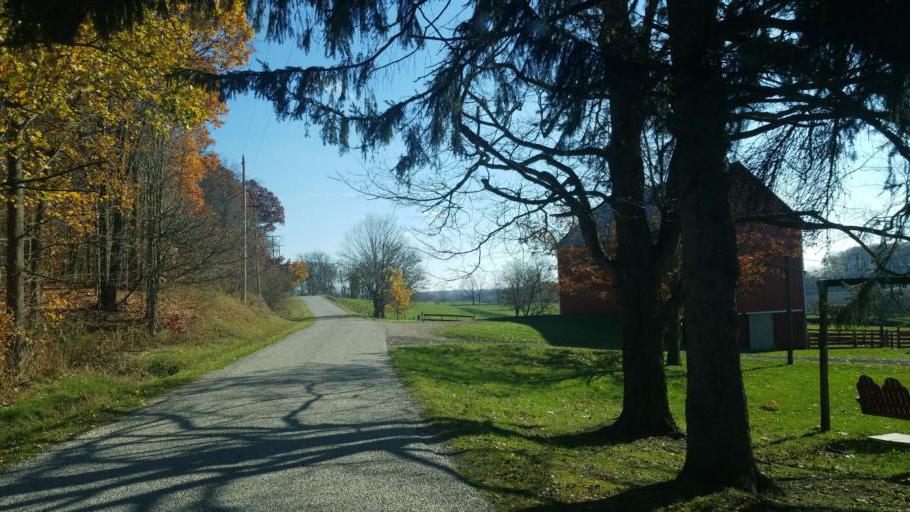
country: US
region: Ohio
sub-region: Ashland County
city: Ashland
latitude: 40.9229
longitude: -82.3139
